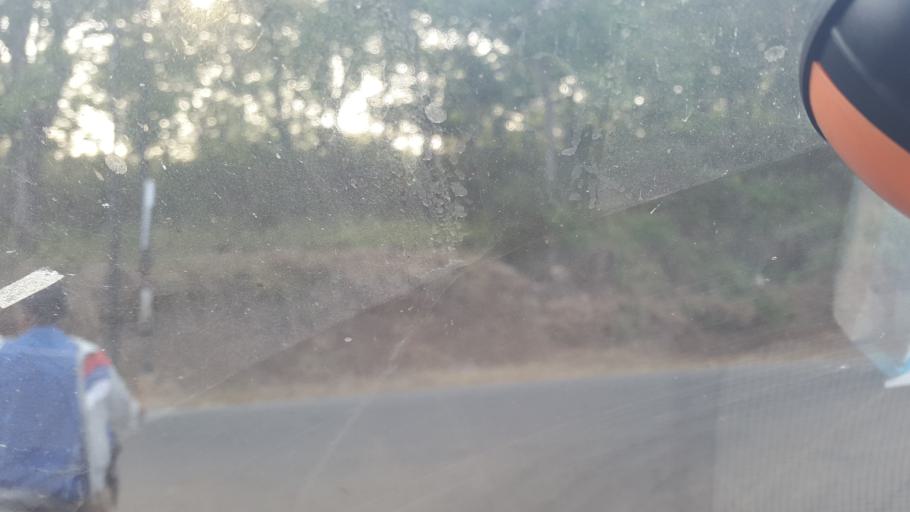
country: ID
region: West Java
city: Cimarelang
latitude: -7.2765
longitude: 106.5348
